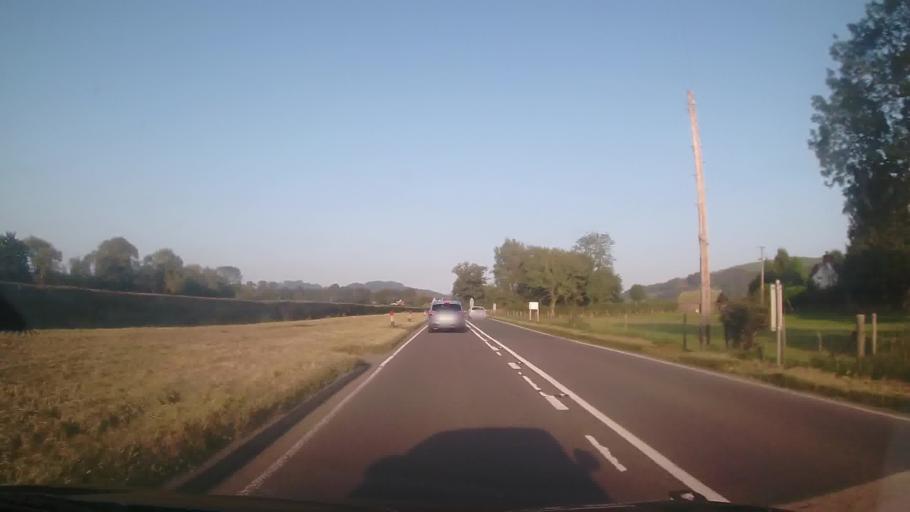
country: GB
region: Wales
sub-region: Sir Powys
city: Mochdre
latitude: 52.5116
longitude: -3.4218
